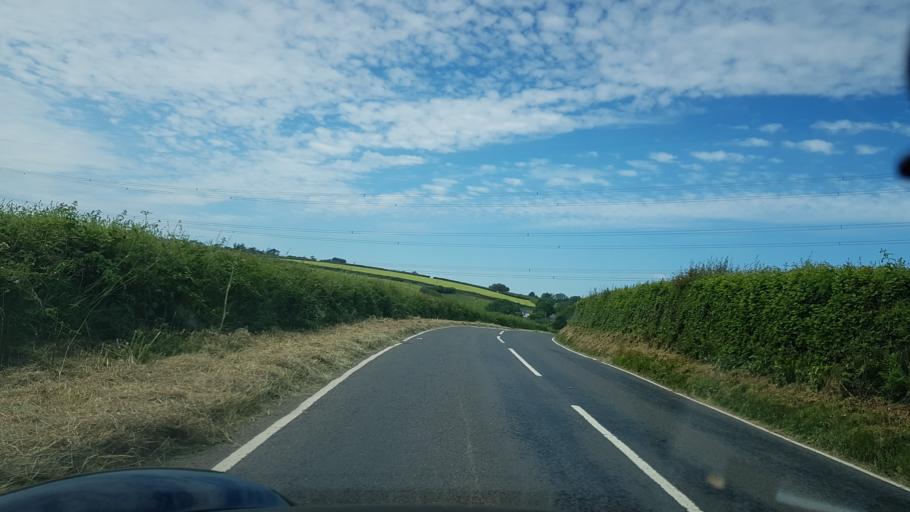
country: GB
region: Wales
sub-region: Carmarthenshire
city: Whitland
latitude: 51.7793
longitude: -4.6238
